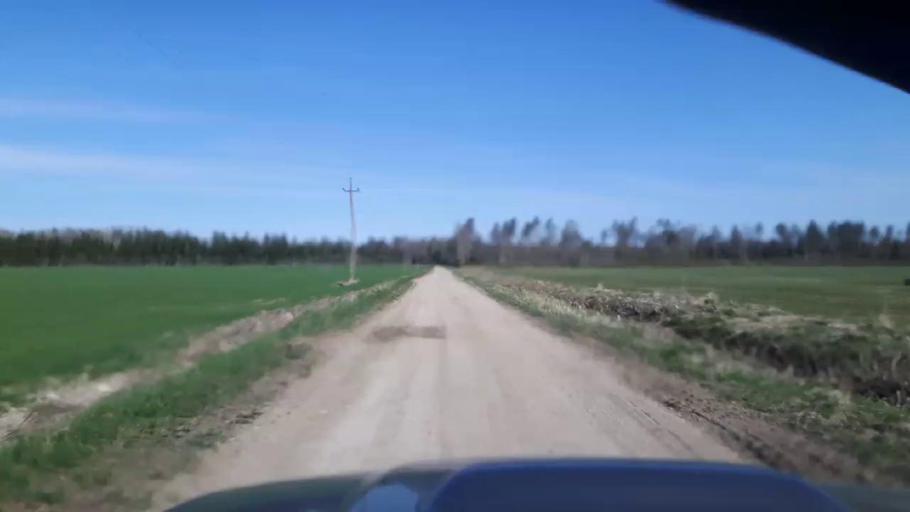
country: EE
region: Paernumaa
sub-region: Tootsi vald
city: Tootsi
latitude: 58.5122
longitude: 24.9311
